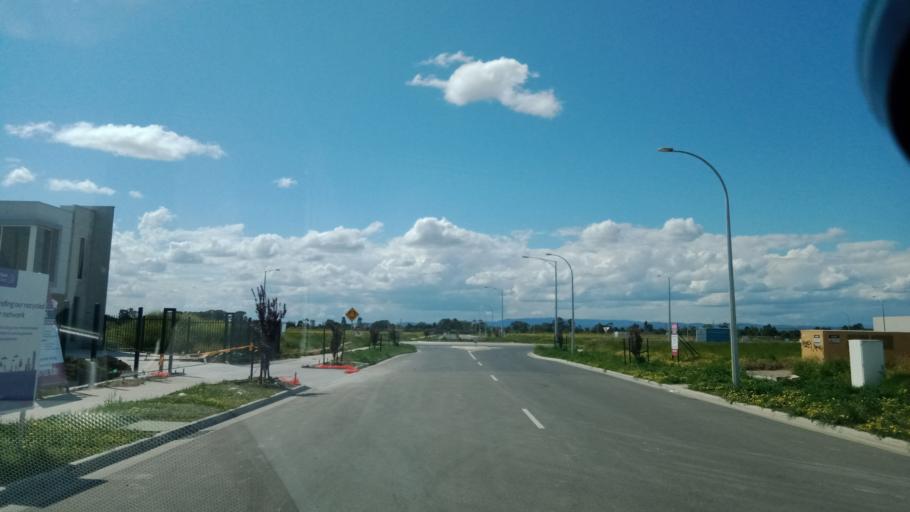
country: AU
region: Victoria
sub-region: Casey
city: Cranbourne West
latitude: -38.0919
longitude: 145.2513
